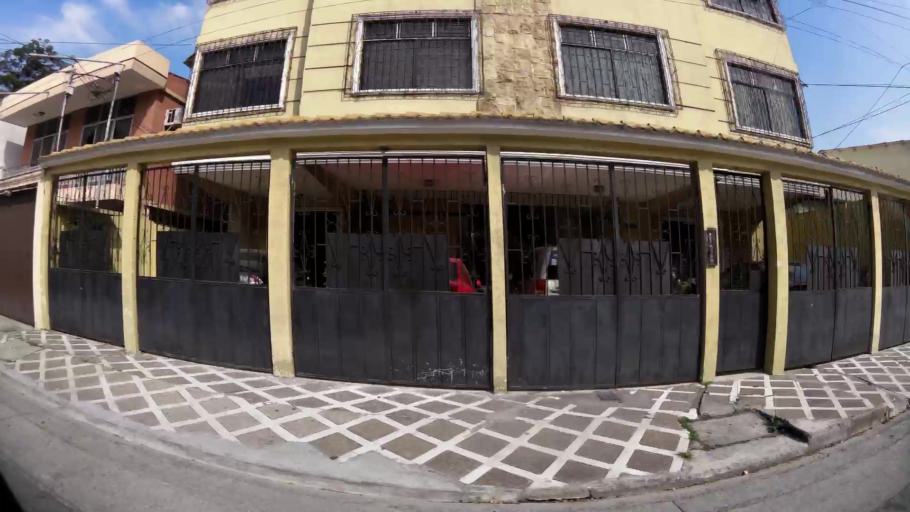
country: EC
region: Guayas
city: Guayaquil
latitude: -2.1857
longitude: -79.9101
